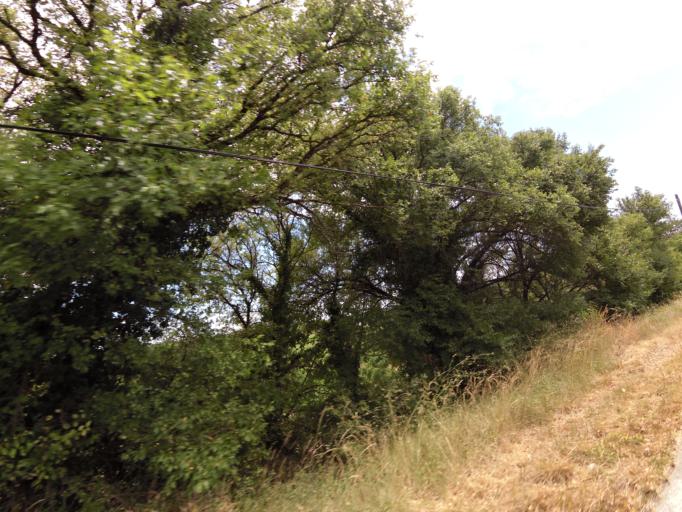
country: FR
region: Languedoc-Roussillon
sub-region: Departement du Gard
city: Quissac
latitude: 43.8901
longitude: 4.0017
